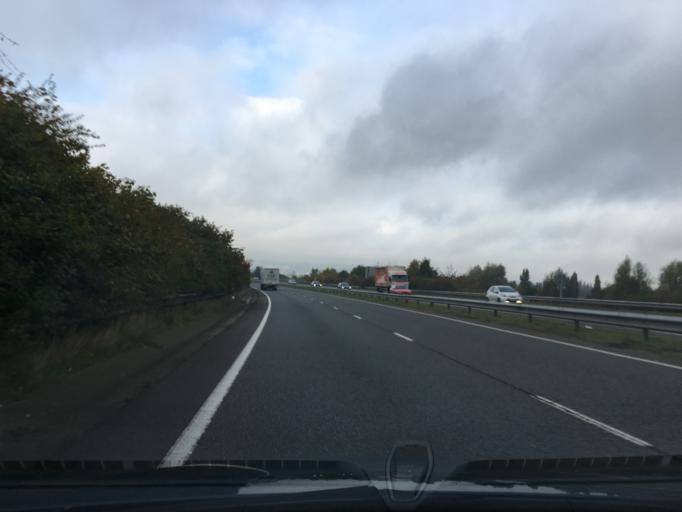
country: GB
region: England
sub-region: Surrey
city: Seale
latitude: 51.2271
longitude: -0.7377
